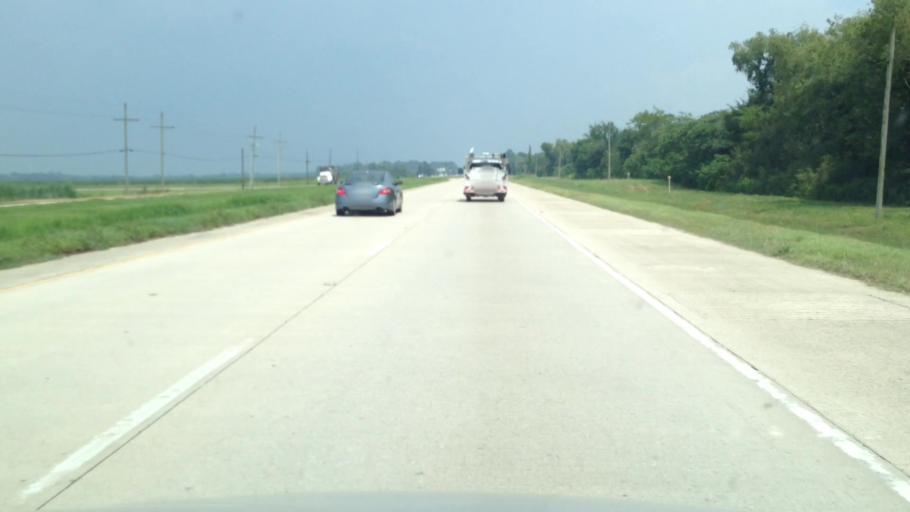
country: US
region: Louisiana
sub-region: West Baton Rouge Parish
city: Port Allen
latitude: 30.4945
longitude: -91.2928
